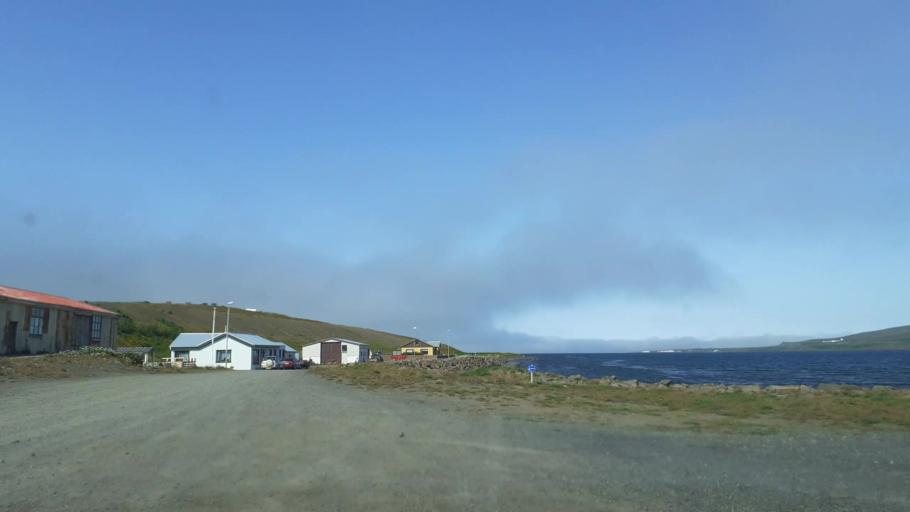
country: IS
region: West
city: Borgarnes
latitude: 65.2100
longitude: -21.0921
